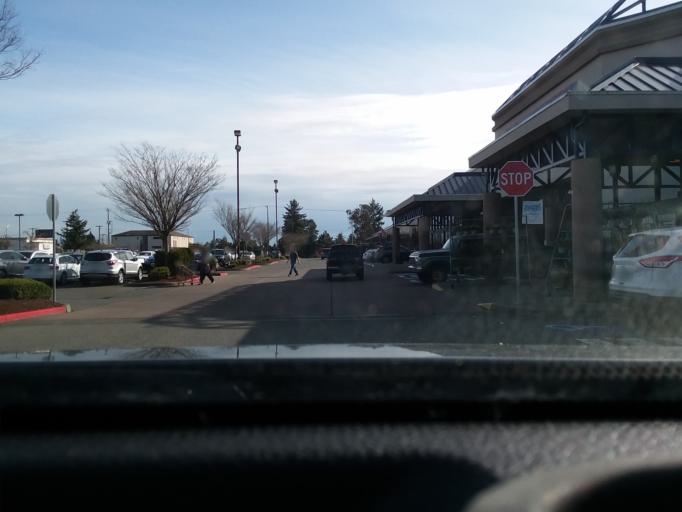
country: US
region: Washington
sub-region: King County
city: Shoreline
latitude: 47.7210
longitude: -122.3466
